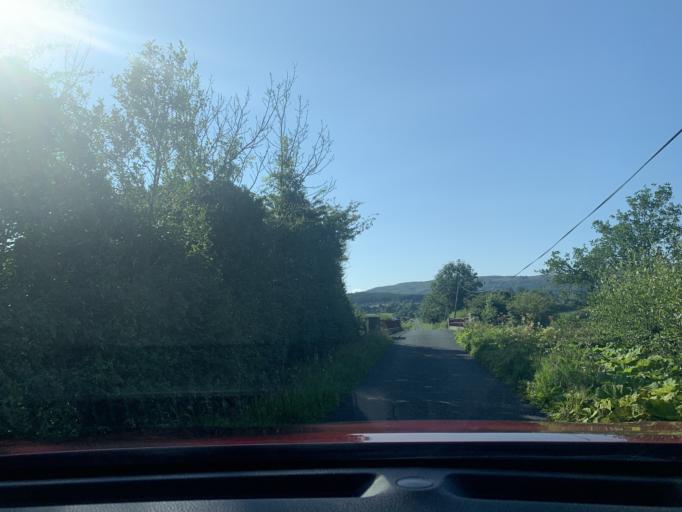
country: IE
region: Connaught
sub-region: Sligo
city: Tobercurry
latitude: 54.0792
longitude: -8.8059
